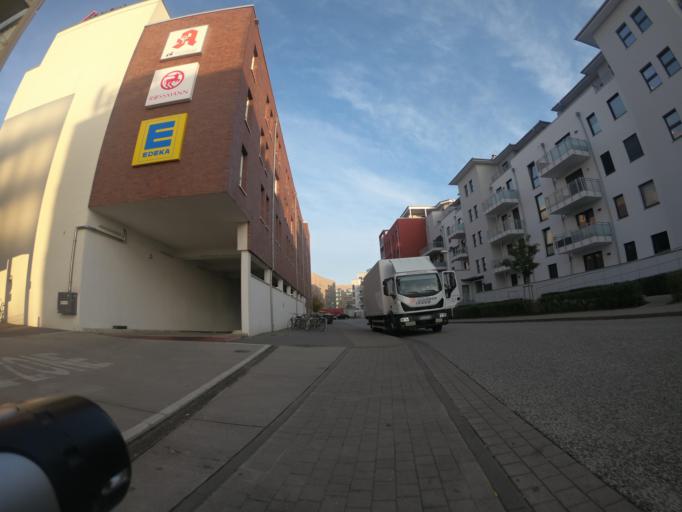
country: DE
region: Mecklenburg-Vorpommern
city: Rostock
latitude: 54.0920
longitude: 12.1511
